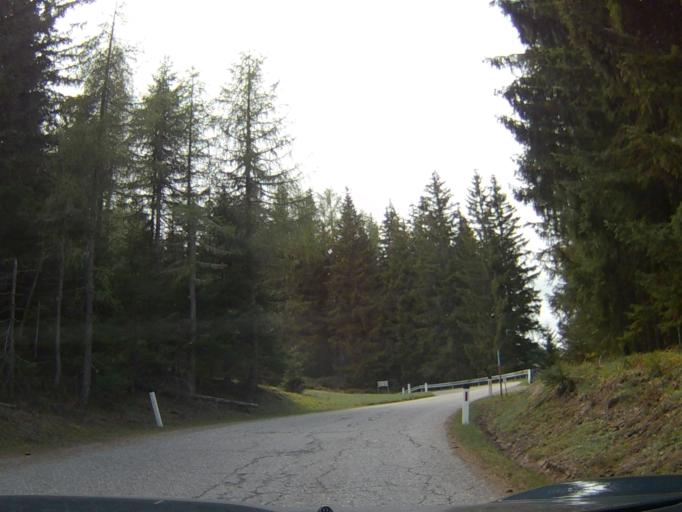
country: AT
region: Carinthia
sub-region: Politischer Bezirk Villach Land
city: Stockenboi
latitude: 46.7432
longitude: 13.5326
